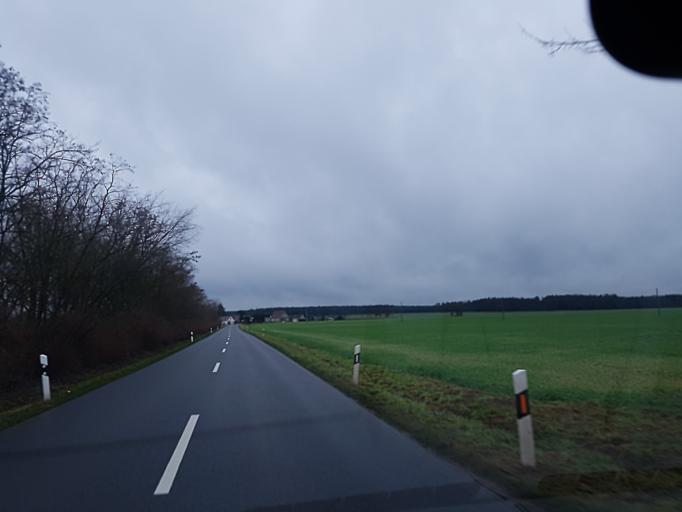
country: DE
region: Brandenburg
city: Finsterwalde
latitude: 51.6095
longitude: 13.6618
